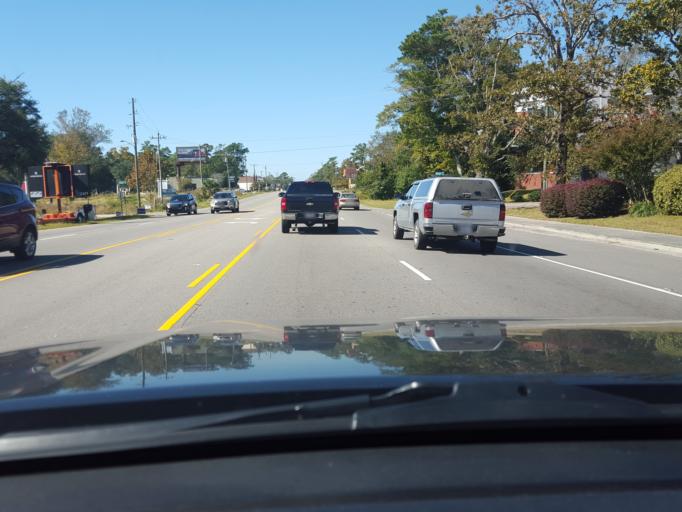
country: US
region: North Carolina
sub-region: New Hanover County
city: Seagate
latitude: 34.2099
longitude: -77.8387
